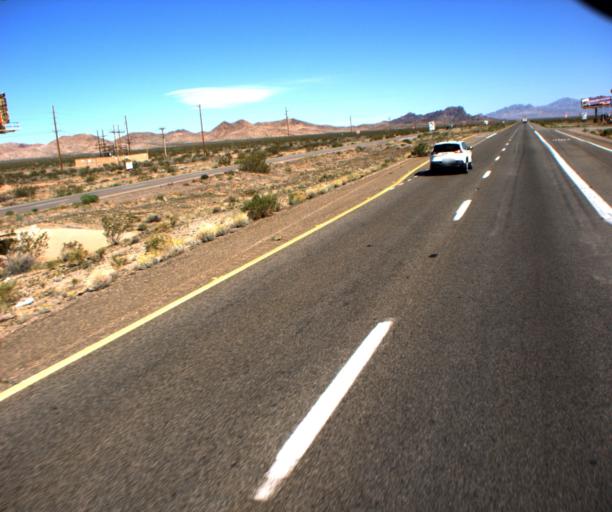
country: US
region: Arizona
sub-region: Mohave County
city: Dolan Springs
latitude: 35.7210
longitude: -114.4857
